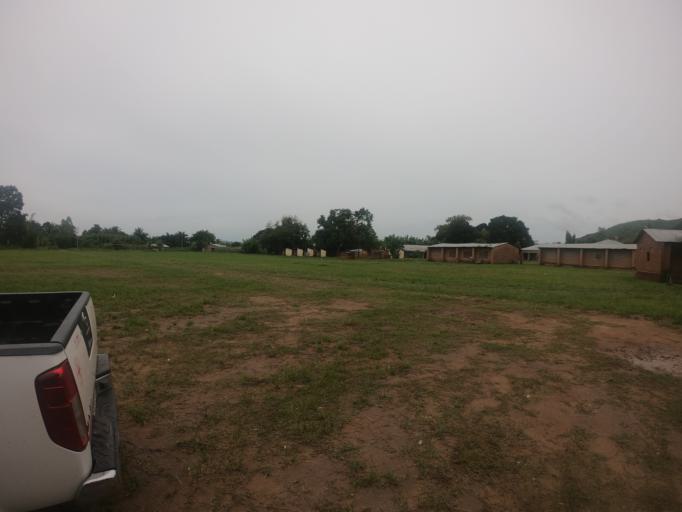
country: TZ
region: Mbeya
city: Kyela
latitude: -9.6455
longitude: 33.8139
